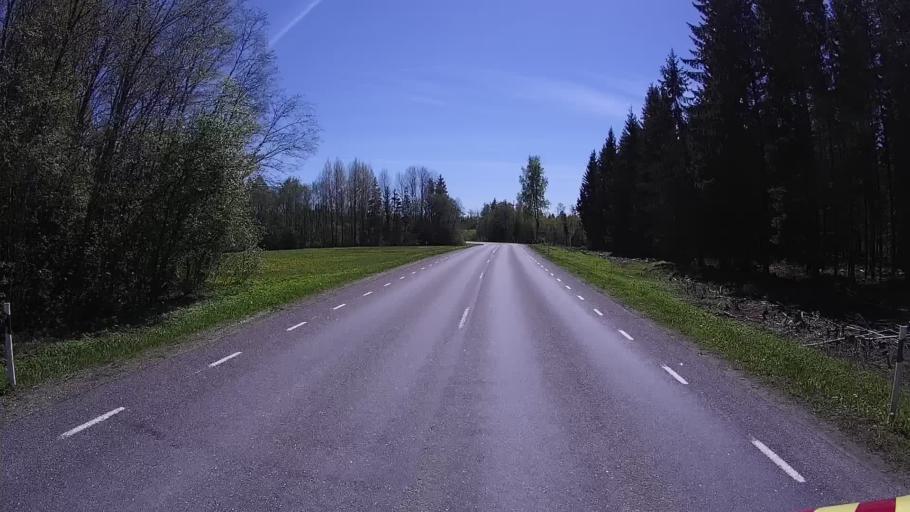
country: EE
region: Raplamaa
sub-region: Kehtna vald
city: Kehtna
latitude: 59.0488
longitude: 25.0236
